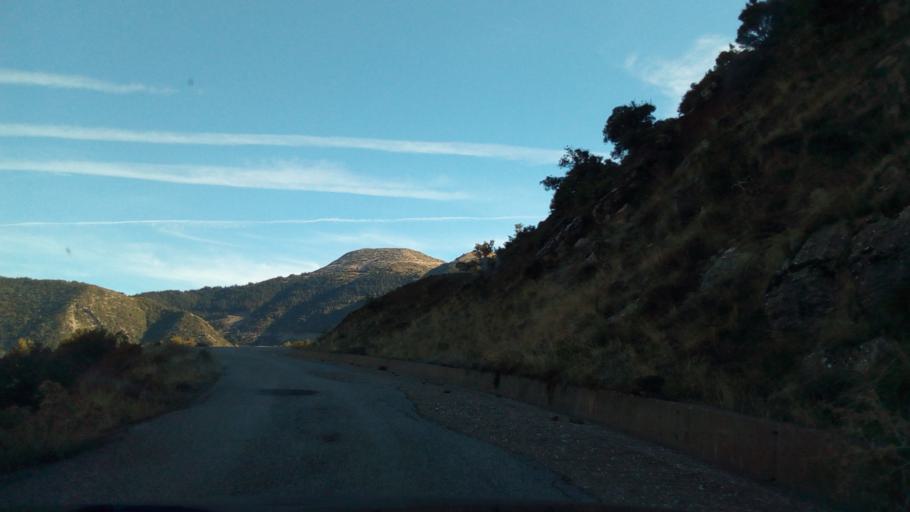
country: GR
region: West Greece
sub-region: Nomos Aitolias kai Akarnanias
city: Nafpaktos
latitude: 38.5091
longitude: 21.8367
